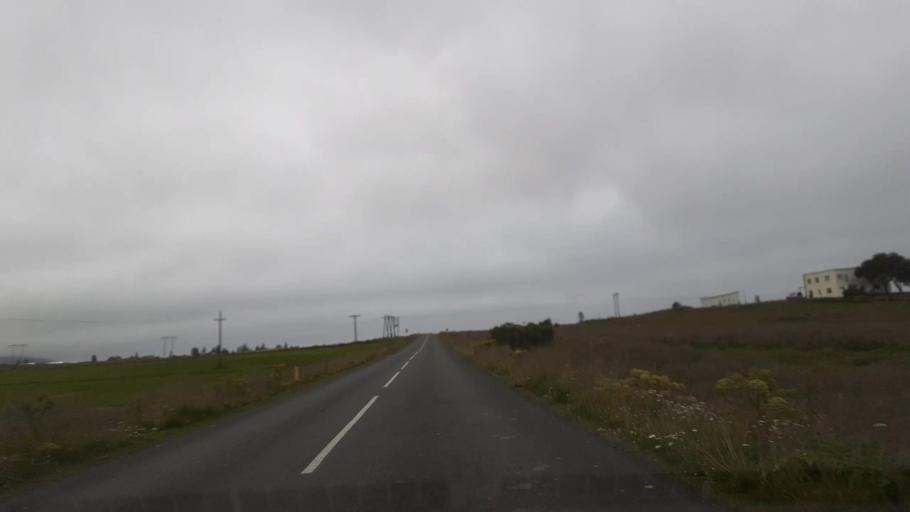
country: IS
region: Northeast
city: Dalvik
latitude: 65.9600
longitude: -18.5445
